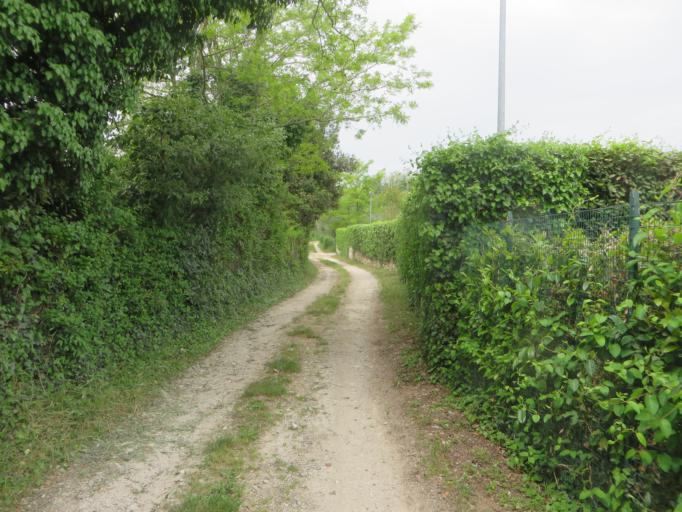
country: IT
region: Lombardy
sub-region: Provincia di Brescia
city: San Felice del Benaco
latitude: 45.5903
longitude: 10.5683
